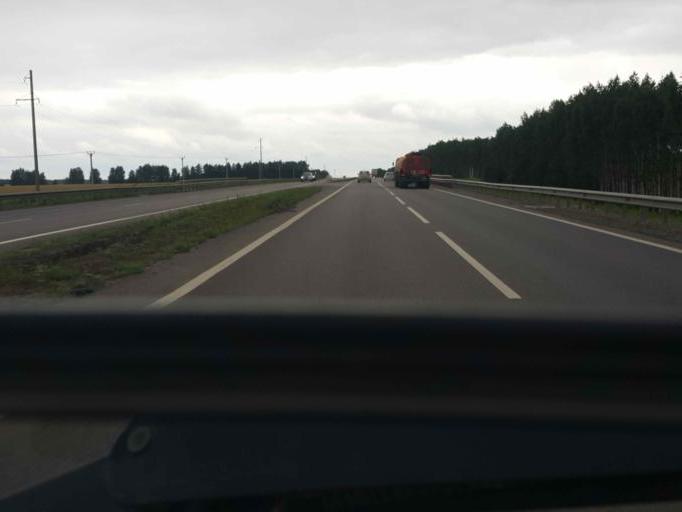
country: RU
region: Tambov
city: Zavoronezhskoye
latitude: 52.8787
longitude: 40.7430
